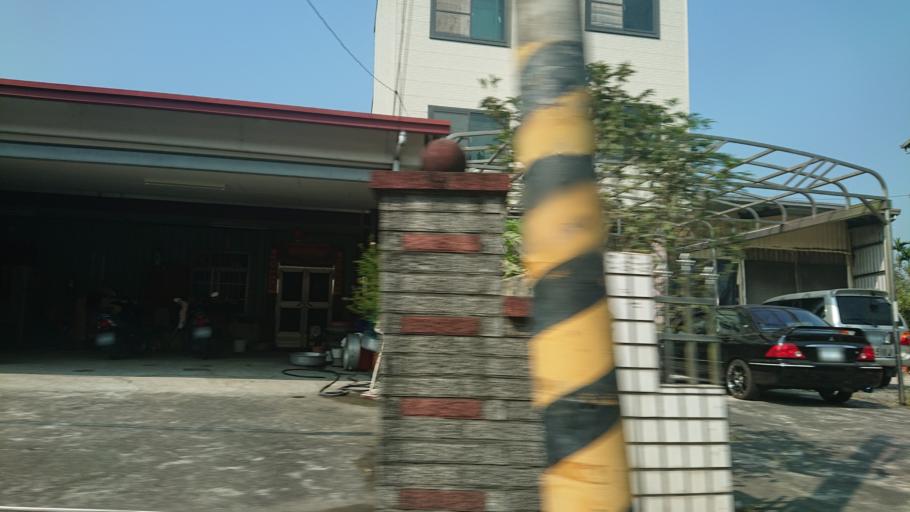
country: TW
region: Taiwan
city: Lugu
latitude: 23.7023
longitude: 120.6631
